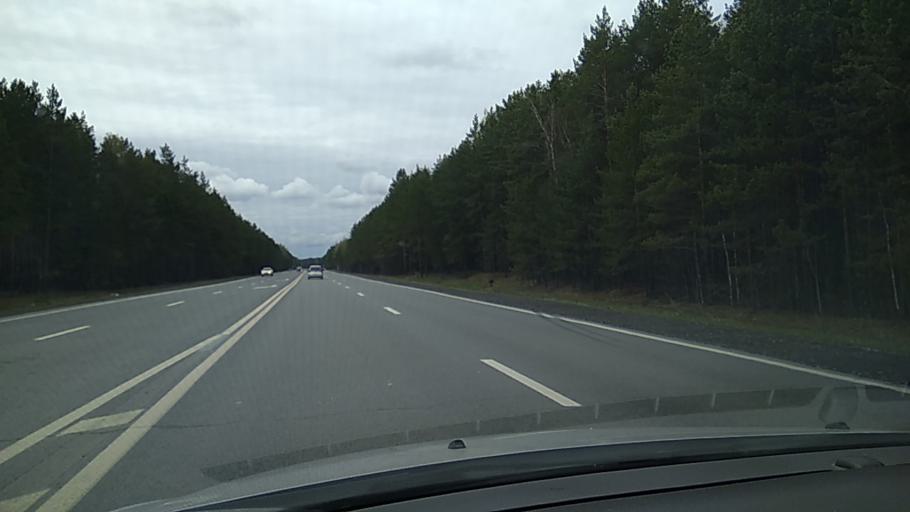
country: RU
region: Tjumen
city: Tyumen
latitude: 57.0745
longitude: 65.5148
